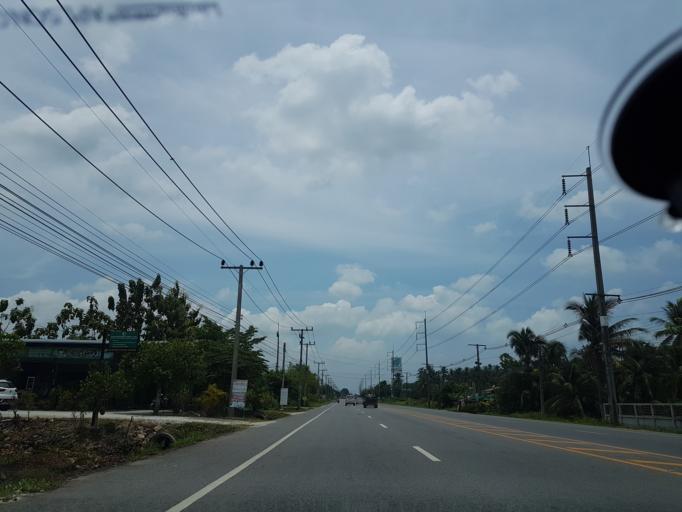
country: TH
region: Songkhla
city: Songkhla
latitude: 7.0971
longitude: 100.6341
